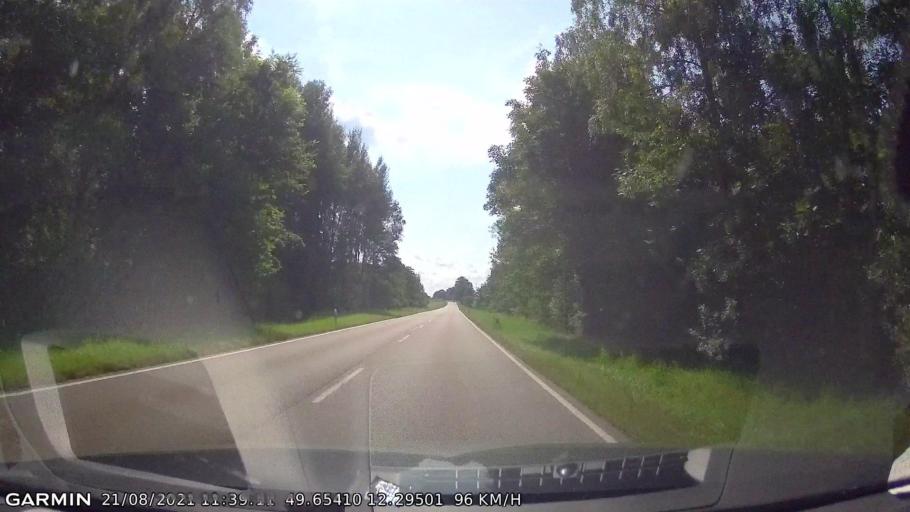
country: DE
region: Bavaria
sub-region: Upper Palatinate
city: Waldthurn
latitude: 49.6541
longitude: 12.2950
